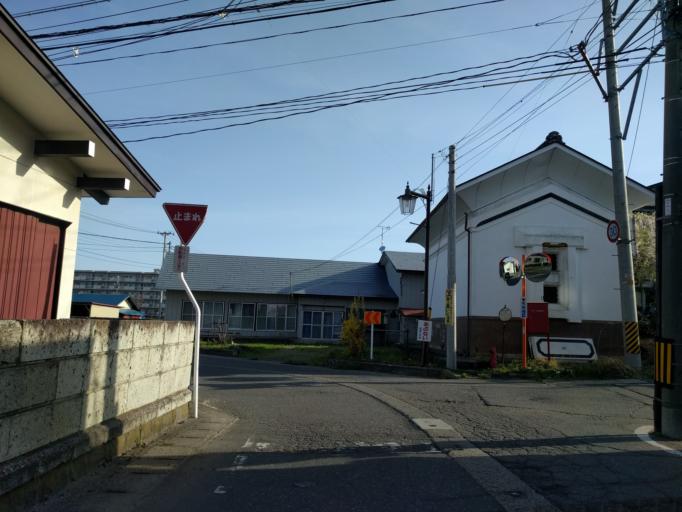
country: JP
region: Fukushima
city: Inawashiro
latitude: 37.5399
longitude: 140.1374
